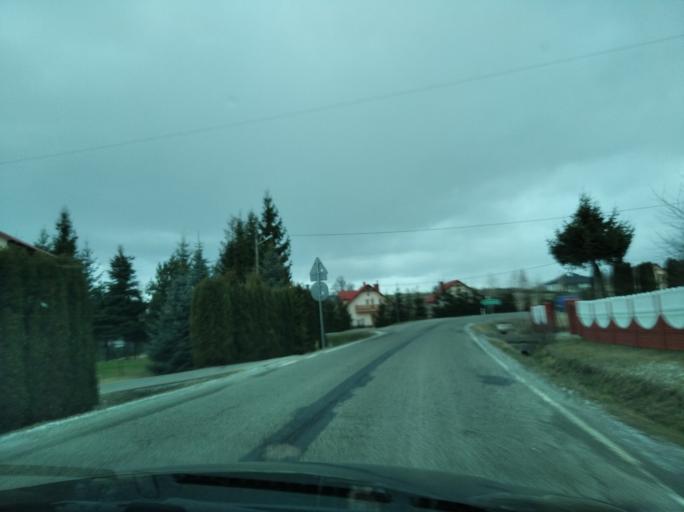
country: PL
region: Subcarpathian Voivodeship
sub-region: Powiat rzeszowski
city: Hyzne
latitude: 49.9315
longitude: 22.1860
